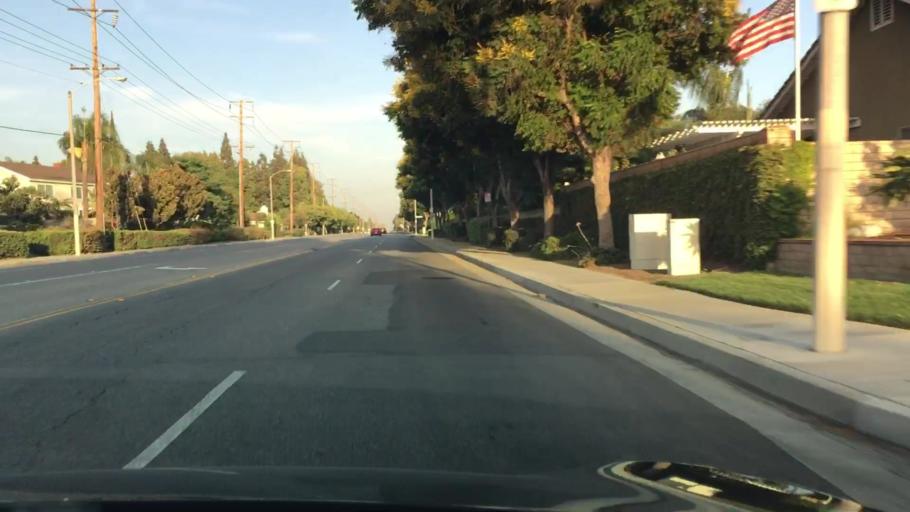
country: US
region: California
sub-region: San Bernardino County
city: Ontario
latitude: 34.0266
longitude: -117.6457
